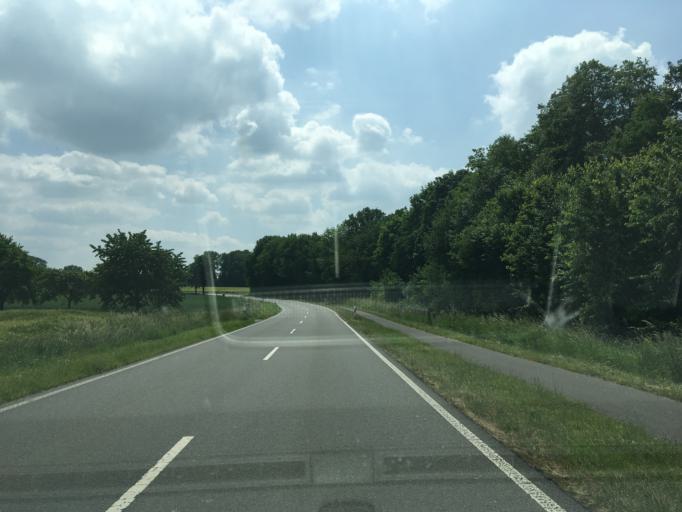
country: DE
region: North Rhine-Westphalia
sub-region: Regierungsbezirk Munster
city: Rhede
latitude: 51.8183
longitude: 6.7735
